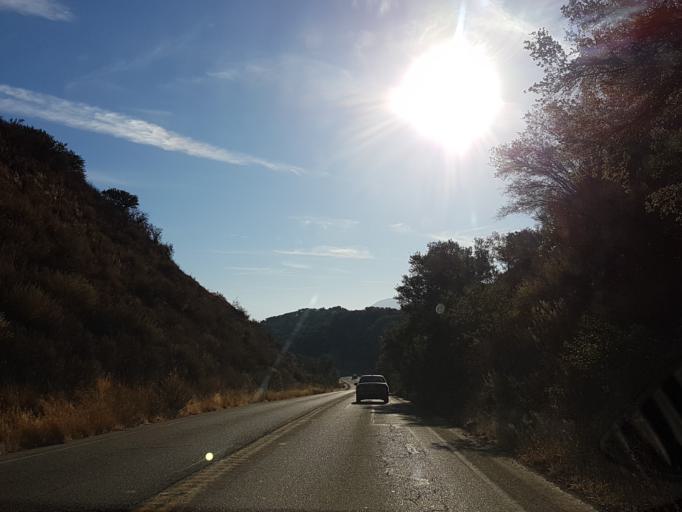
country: US
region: California
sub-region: Santa Barbara County
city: Santa Ynez
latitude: 34.5622
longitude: -119.9284
